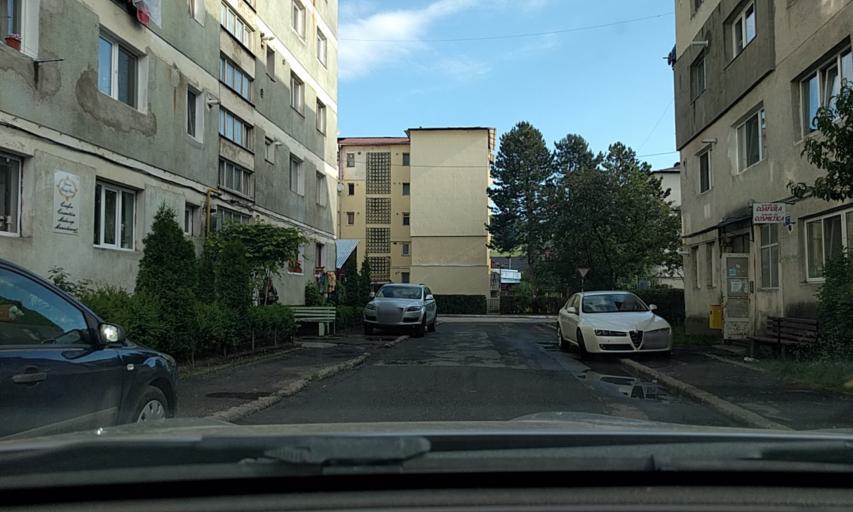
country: RO
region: Bistrita-Nasaud
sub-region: Oras Nasaud
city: Nasaud
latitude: 47.2822
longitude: 24.4134
